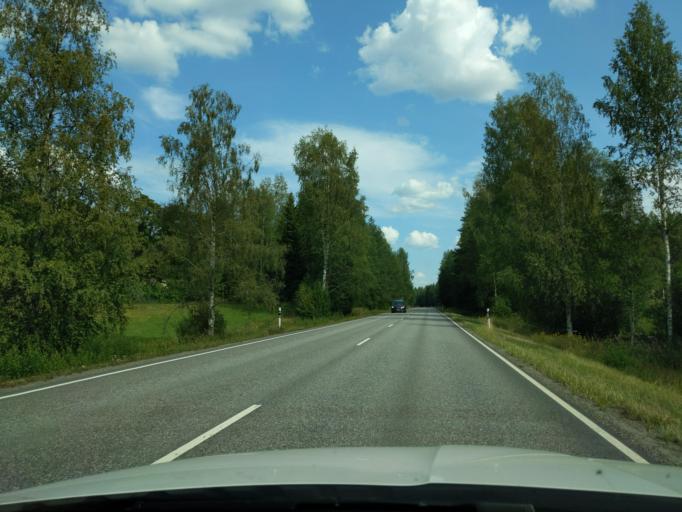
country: FI
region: Haeme
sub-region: Haemeenlinna
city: Lammi
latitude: 61.1813
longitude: 25.0545
